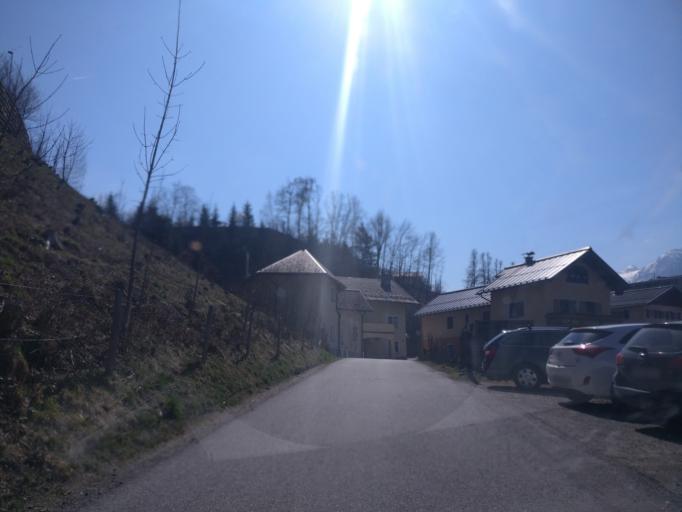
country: AT
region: Salzburg
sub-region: Politischer Bezirk Sankt Johann im Pongau
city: Sankt Johann im Pongau
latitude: 47.3535
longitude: 13.2071
